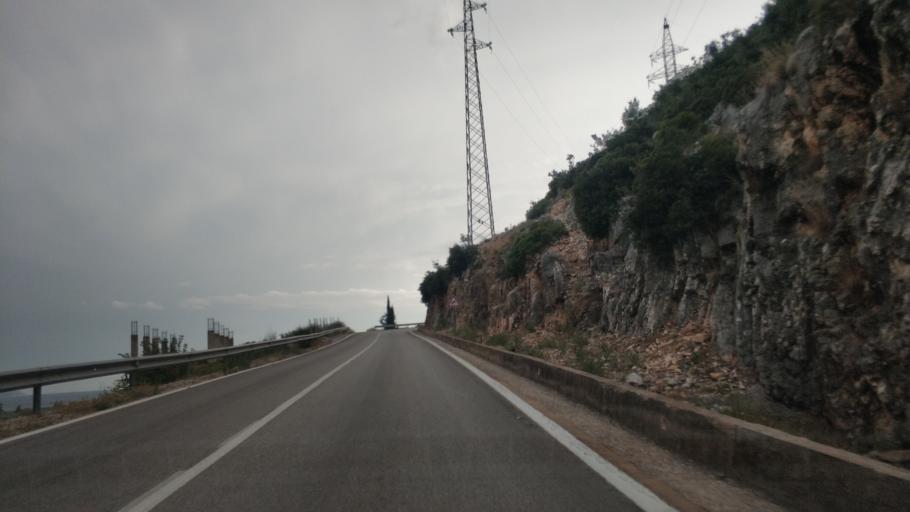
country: AL
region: Vlore
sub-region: Rrethi i Sarandes
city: Lukove
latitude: 40.0608
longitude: 19.8486
